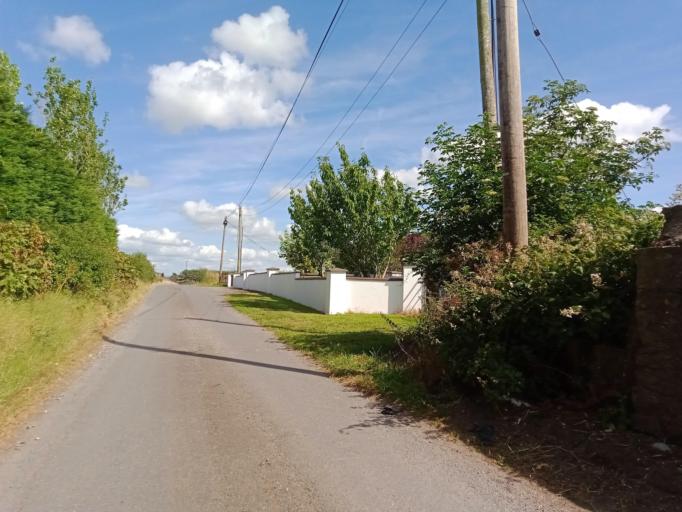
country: IE
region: Leinster
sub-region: Kilkenny
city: Kilkenny
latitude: 52.6369
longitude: -7.2115
